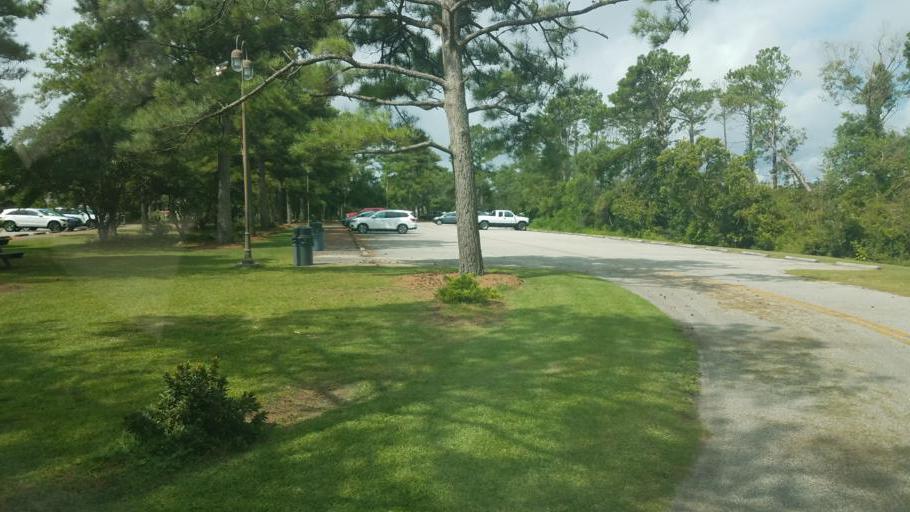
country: US
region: North Carolina
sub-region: Dare County
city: Manteo
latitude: 35.9122
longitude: -75.6650
